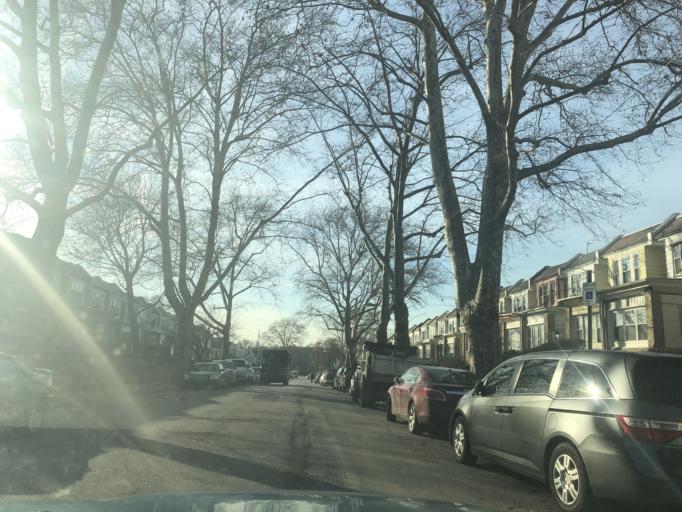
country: US
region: Pennsylvania
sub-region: Montgomery County
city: Bala-Cynwyd
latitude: 39.9856
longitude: -75.2332
